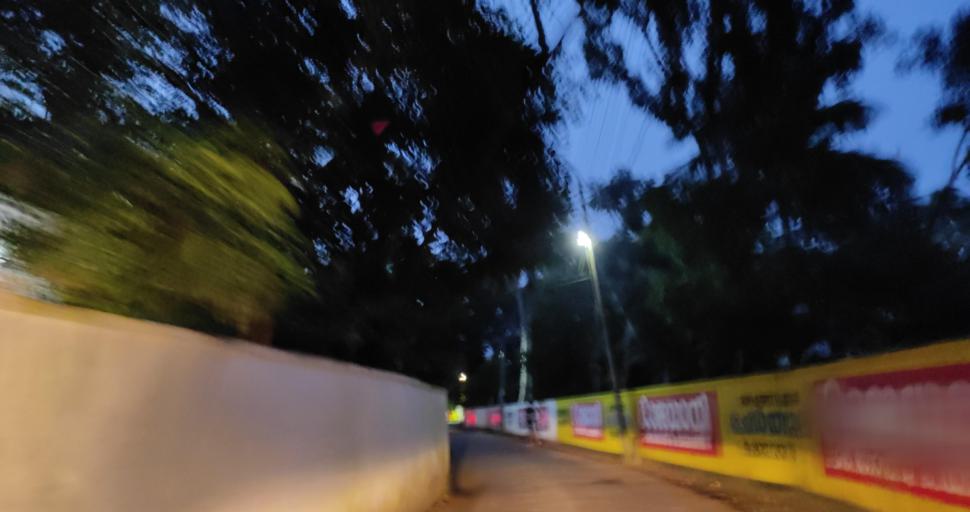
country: IN
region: Kerala
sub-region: Alappuzha
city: Vayalar
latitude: 9.7263
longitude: 76.2908
